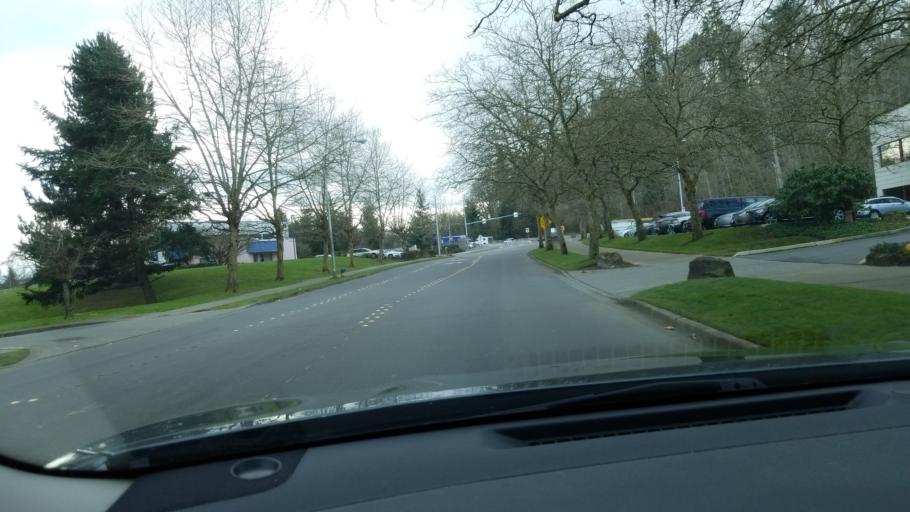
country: US
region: Washington
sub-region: King County
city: Tukwila
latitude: 47.4671
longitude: -122.2480
